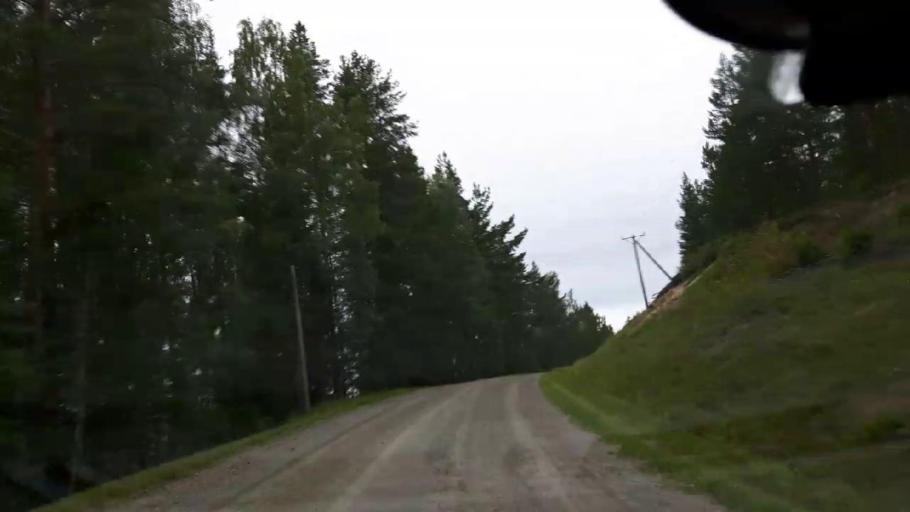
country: SE
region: Vaesternorrland
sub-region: Ange Kommun
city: Fransta
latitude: 62.7948
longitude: 16.0321
